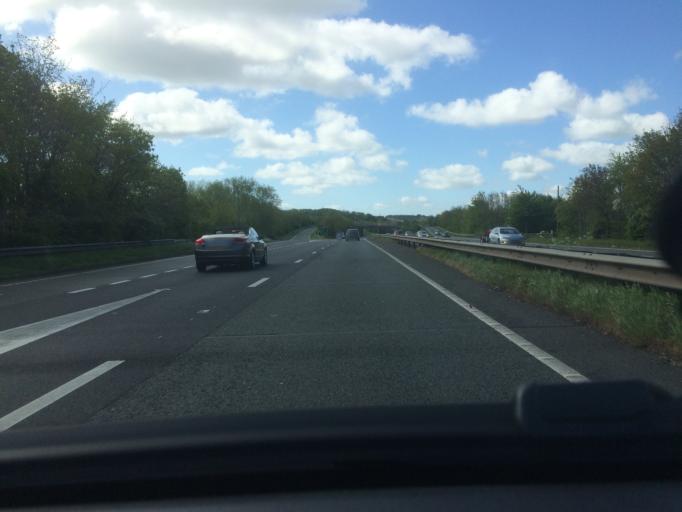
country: GB
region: Wales
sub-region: Wrexham
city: Rossett
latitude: 53.1090
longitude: -2.9550
